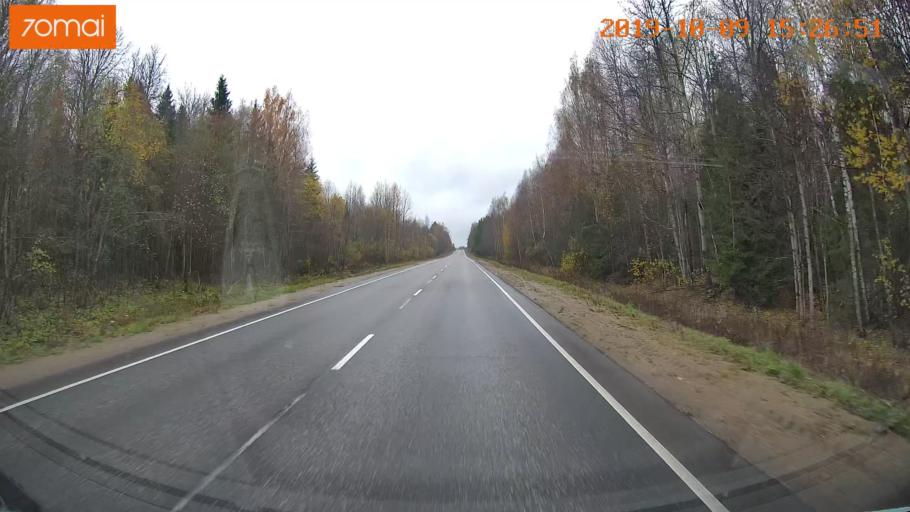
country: RU
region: Kostroma
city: Susanino
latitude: 58.0172
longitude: 41.3936
